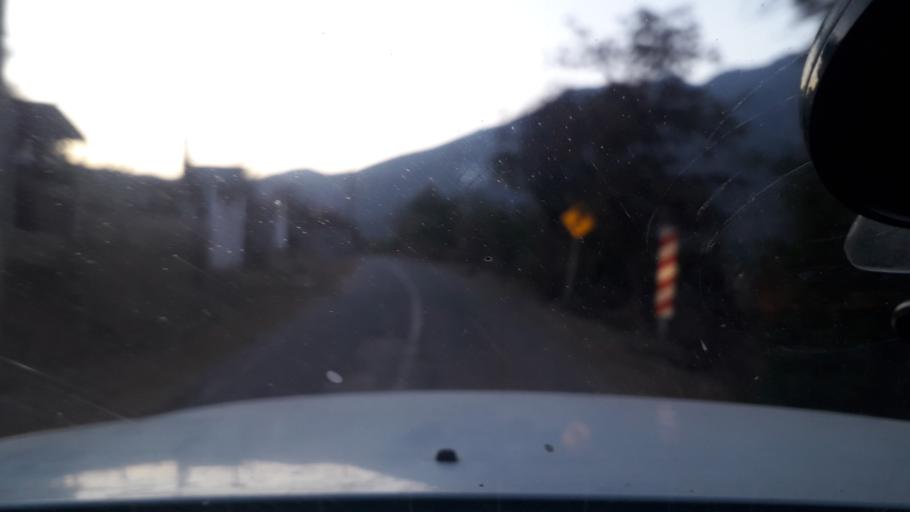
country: CL
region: Valparaiso
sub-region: Provincia de Marga Marga
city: Limache
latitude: -33.1783
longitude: -71.1176
